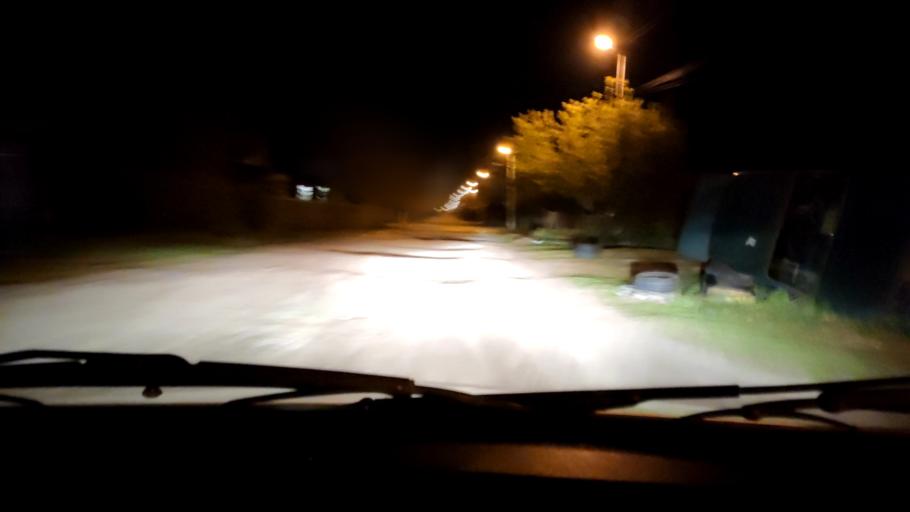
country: RU
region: Voronezj
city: Somovo
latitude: 51.7334
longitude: 39.2680
